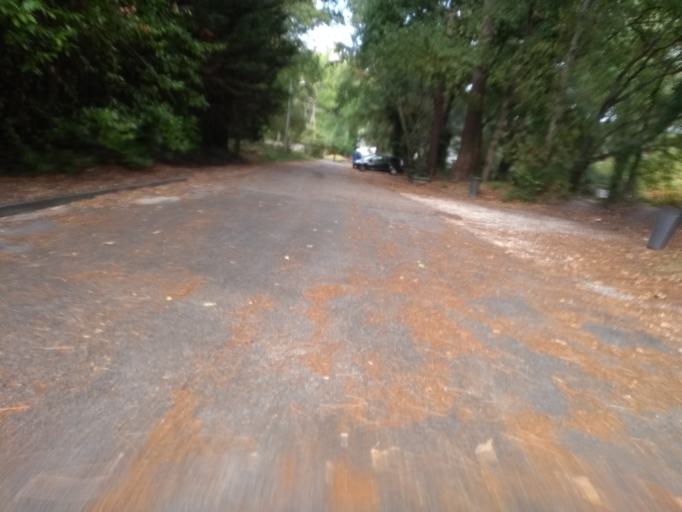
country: FR
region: Aquitaine
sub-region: Departement de la Gironde
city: Gradignan
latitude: 44.7843
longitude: -0.6239
